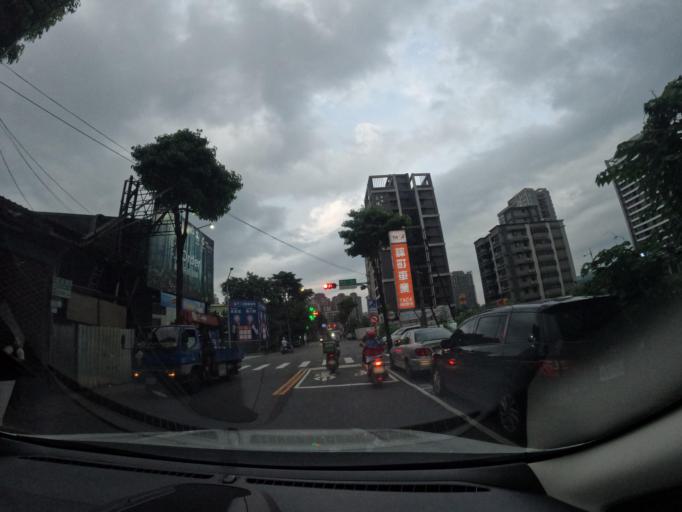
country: TW
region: Taipei
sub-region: Taipei
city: Banqiao
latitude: 24.9787
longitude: 121.4461
